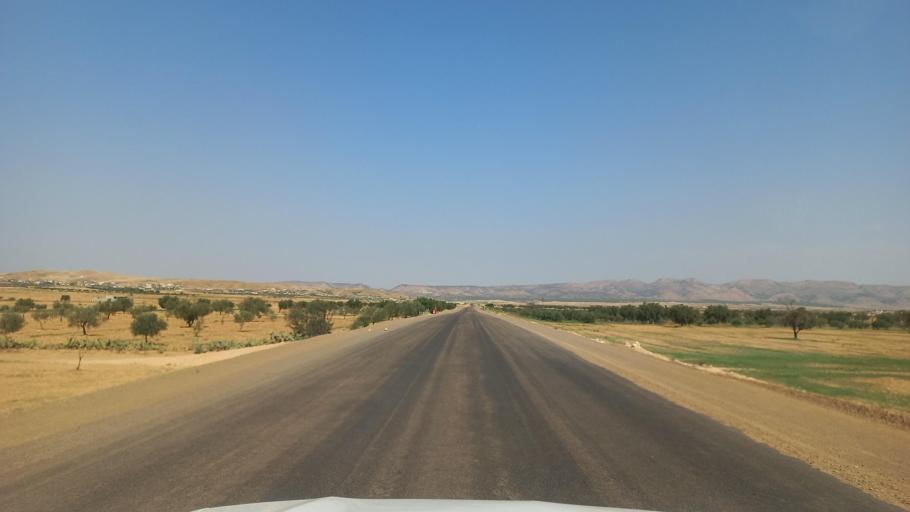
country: TN
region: Al Qasrayn
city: Sbiba
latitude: 35.3636
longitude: 9.0429
